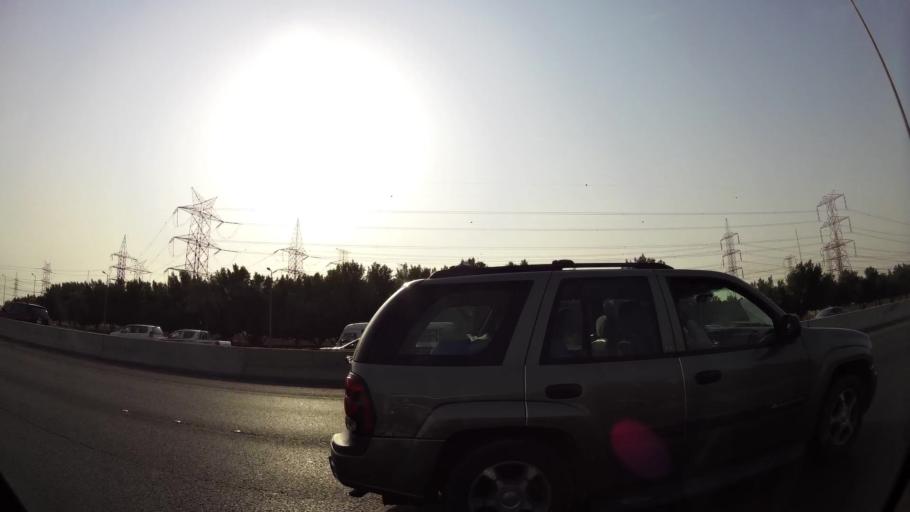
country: KW
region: Mubarak al Kabir
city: Sabah as Salim
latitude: 29.2421
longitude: 48.0494
